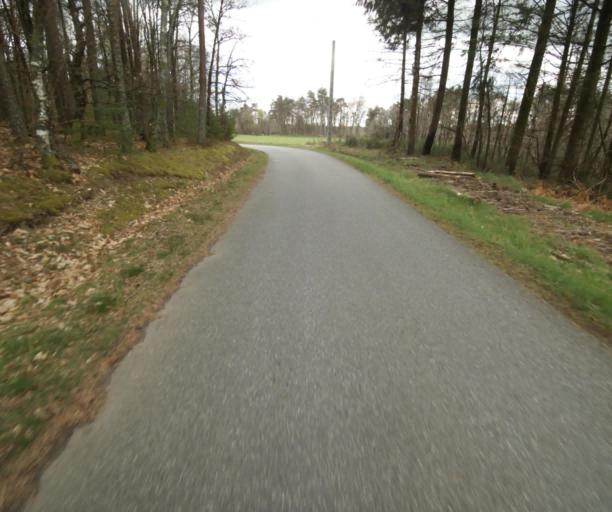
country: FR
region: Limousin
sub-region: Departement de la Correze
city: Correze
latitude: 45.3005
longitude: 1.9218
